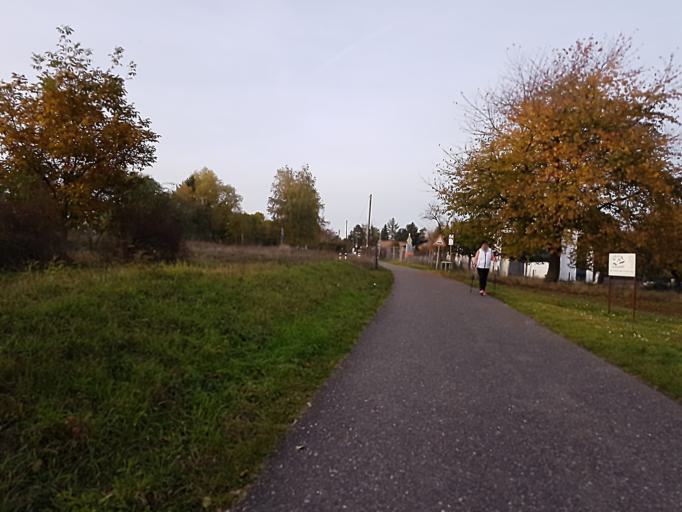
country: DE
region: Bavaria
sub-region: Regierungsbezirk Unterfranken
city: Niedernberg
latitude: 49.8977
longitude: 9.1440
